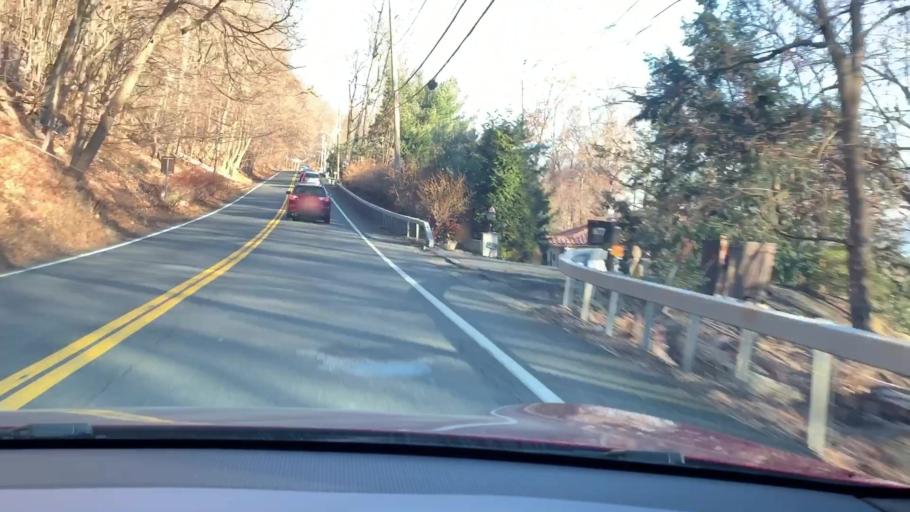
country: US
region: New York
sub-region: Rockland County
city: Piermont
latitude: 41.0534
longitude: -73.9228
